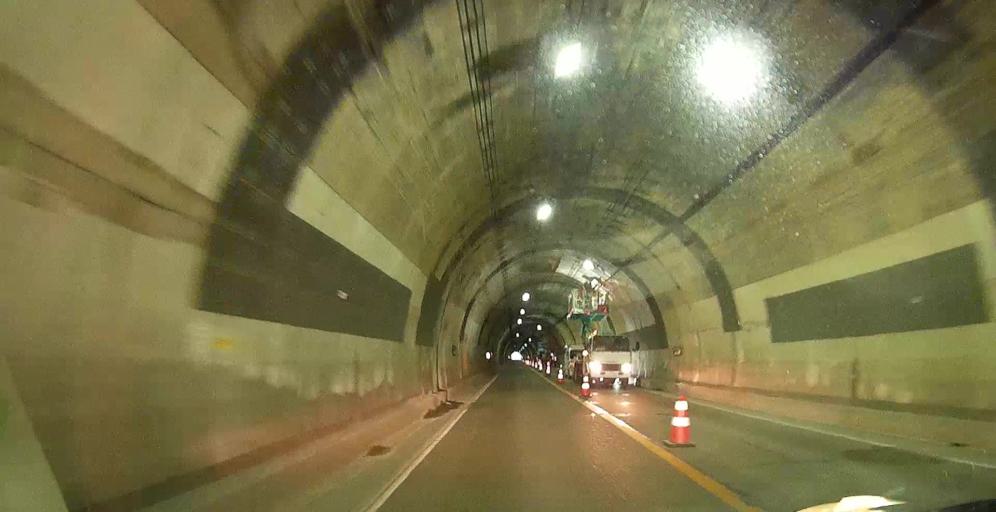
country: JP
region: Kumamoto
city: Yatsushiro
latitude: 32.3712
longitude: 130.5294
